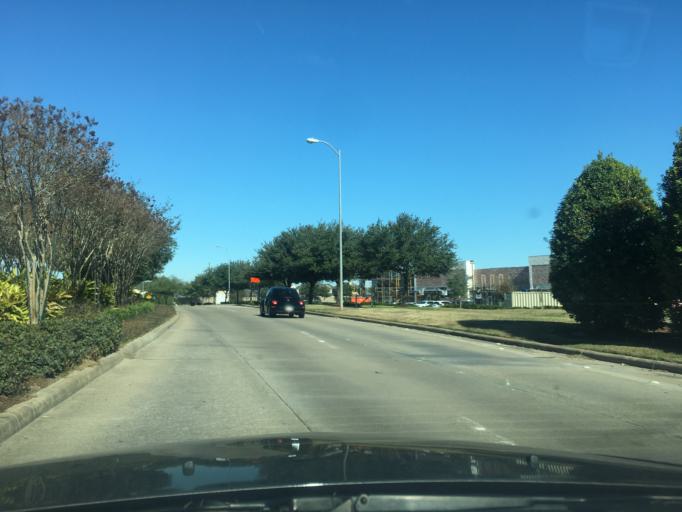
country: US
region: Texas
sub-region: Fort Bend County
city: Greatwood
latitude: 29.5583
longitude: -95.7158
